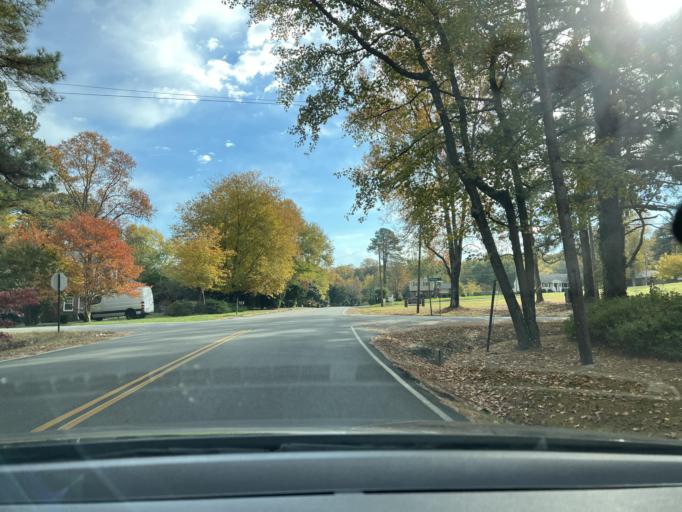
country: US
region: Virginia
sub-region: Henrico County
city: Tuckahoe
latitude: 37.6126
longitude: -77.5415
